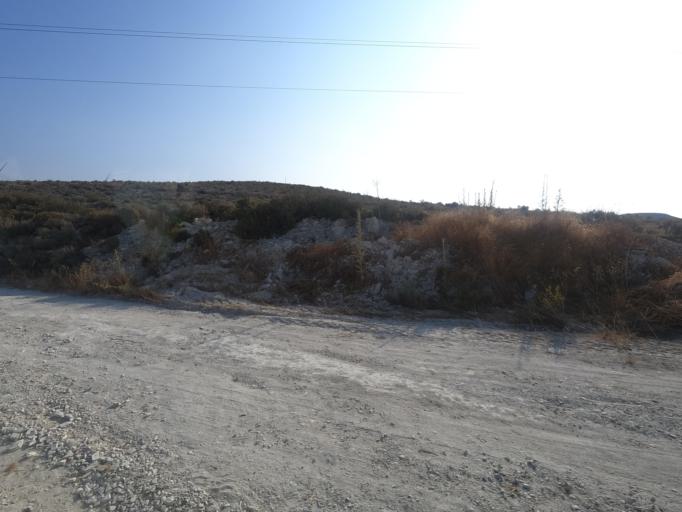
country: CY
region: Larnaka
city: Psevdas
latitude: 34.9430
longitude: 33.5061
